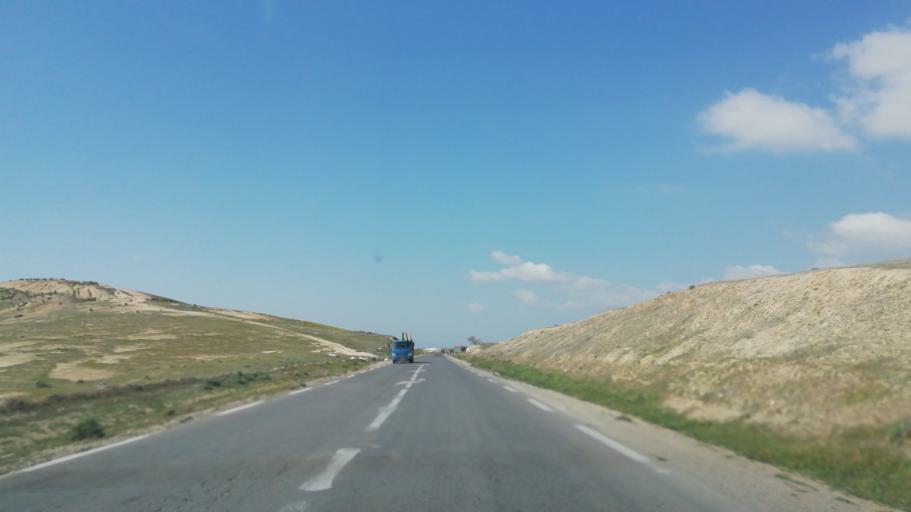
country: DZ
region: Mascara
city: Mascara
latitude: 35.5413
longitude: 0.0935
